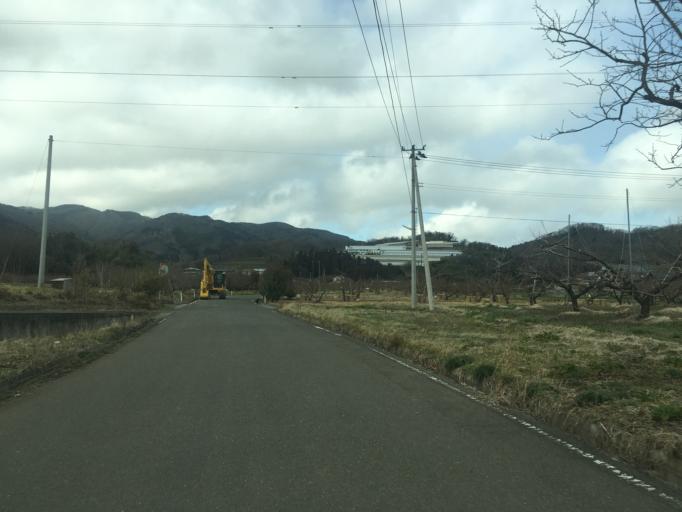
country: JP
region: Fukushima
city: Yanagawamachi-saiwaicho
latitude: 37.8899
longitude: 140.5823
